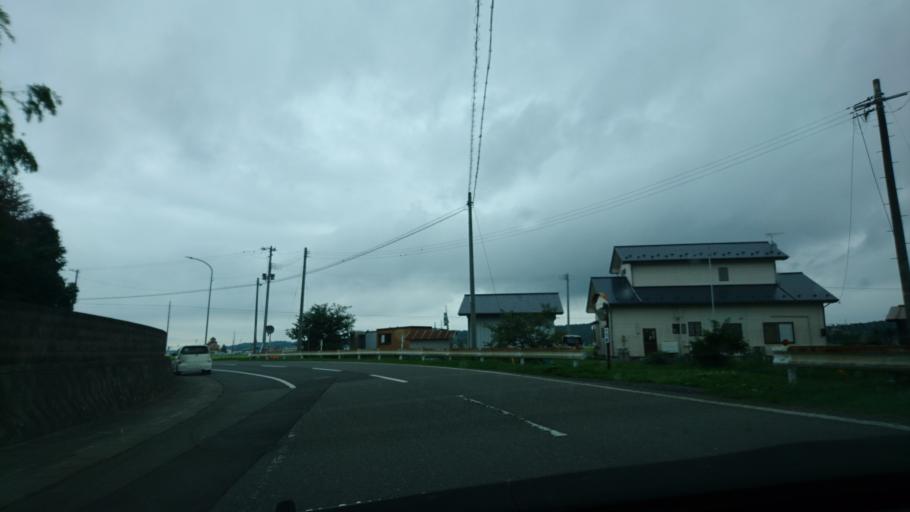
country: JP
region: Iwate
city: Ichinoseki
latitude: 38.8100
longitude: 140.9786
